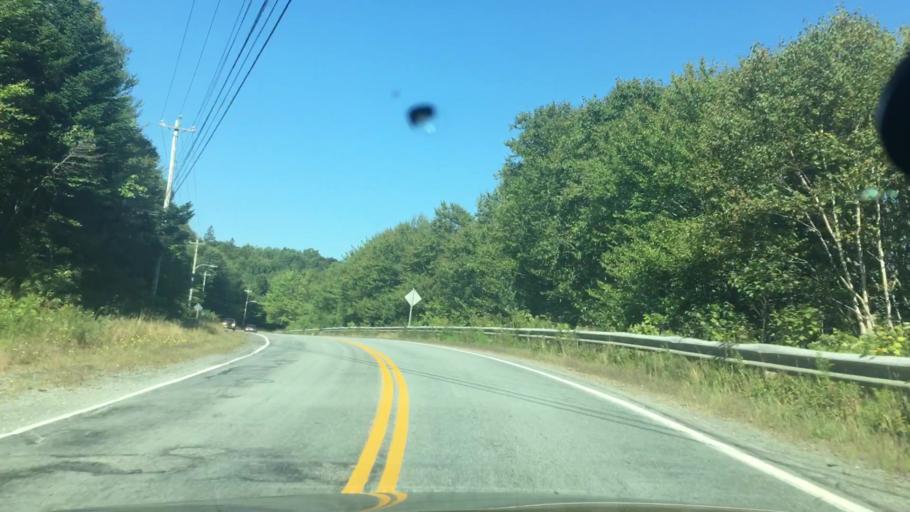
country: CA
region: Nova Scotia
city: New Glasgow
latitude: 44.9173
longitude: -62.5396
